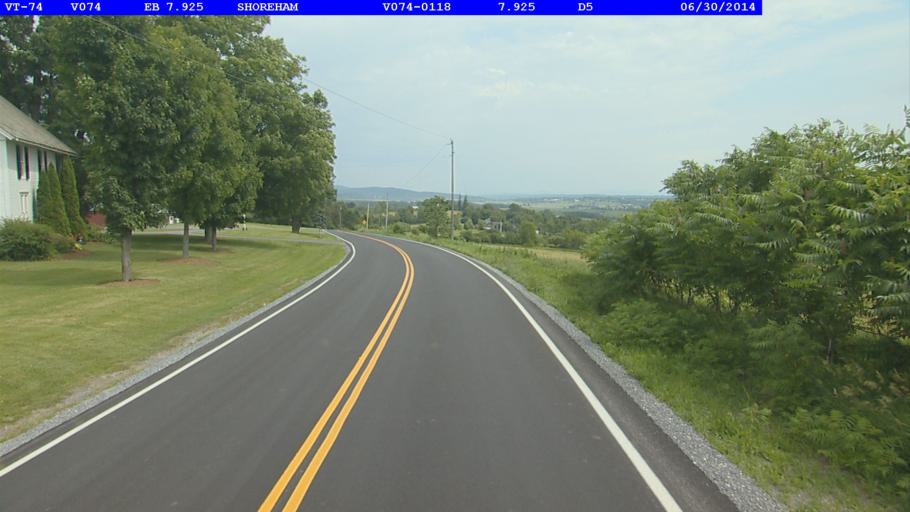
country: US
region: Vermont
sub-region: Addison County
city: Middlebury (village)
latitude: 43.9324
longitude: -73.2876
